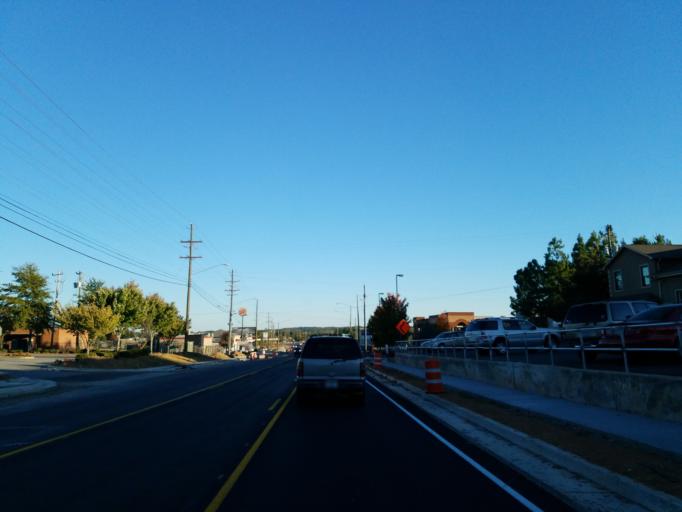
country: US
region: Georgia
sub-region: Dawson County
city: Dawsonville
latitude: 34.3667
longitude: -84.0401
